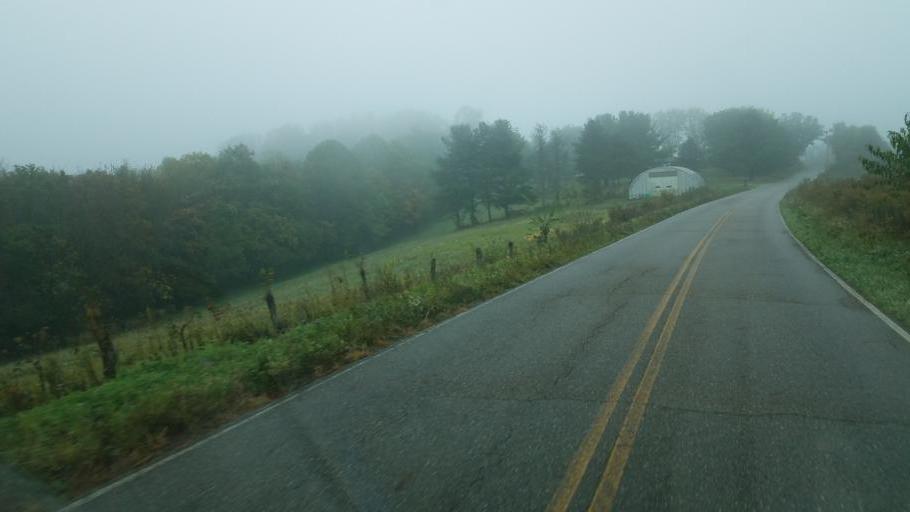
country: US
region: Ohio
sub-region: Harrison County
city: Cadiz
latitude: 40.3821
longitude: -81.1095
